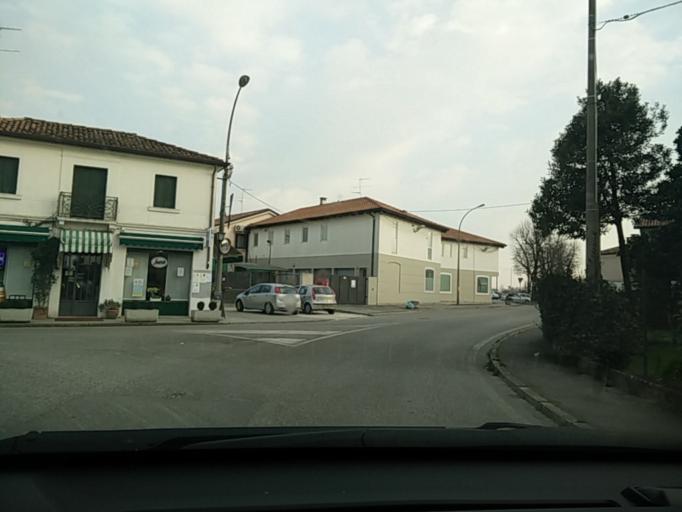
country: IT
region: Veneto
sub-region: Provincia di Treviso
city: Levada
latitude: 45.7619
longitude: 12.4667
